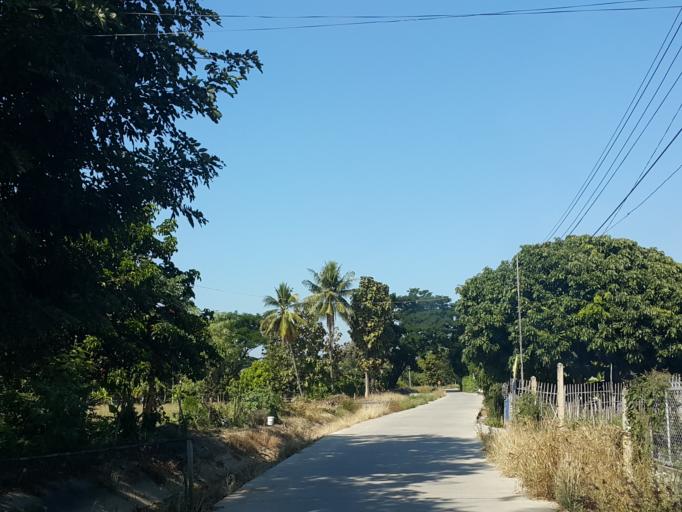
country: TH
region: Chiang Mai
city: San Sai
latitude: 18.8705
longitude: 98.9841
